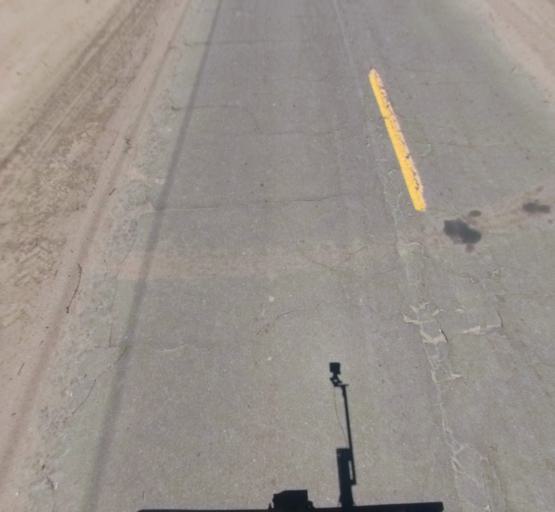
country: US
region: California
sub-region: Madera County
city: Chowchilla
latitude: 37.0545
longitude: -120.3010
